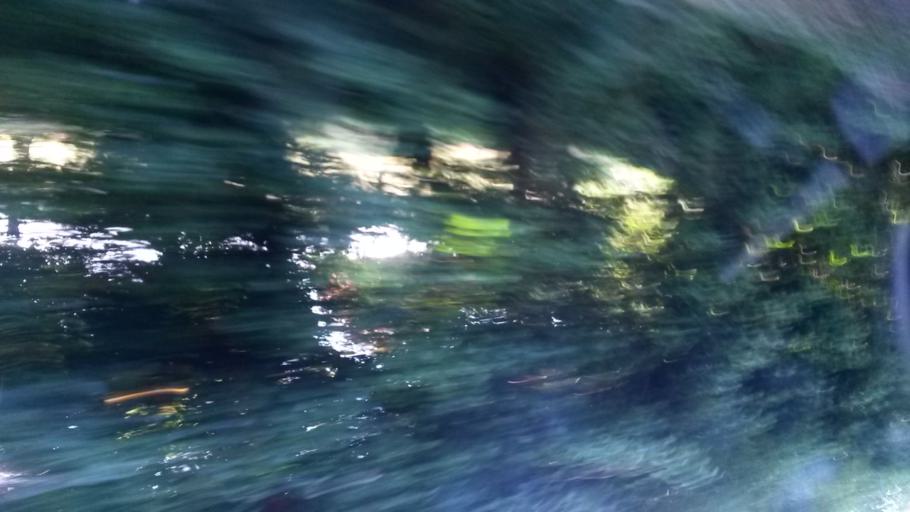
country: IE
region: Leinster
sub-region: Dublin City
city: Finglas
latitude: 53.4605
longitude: -6.3239
